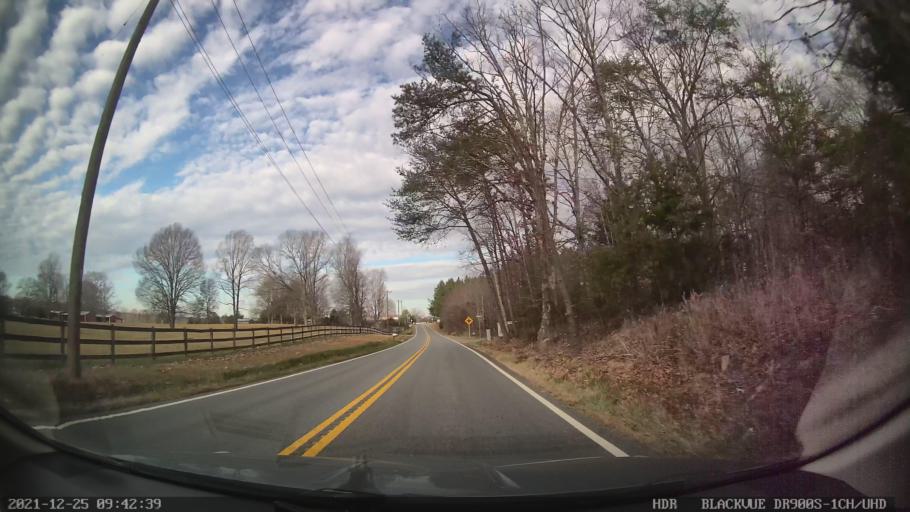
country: US
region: Virginia
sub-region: Goochland County
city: Goochland
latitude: 37.8271
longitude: -77.8928
